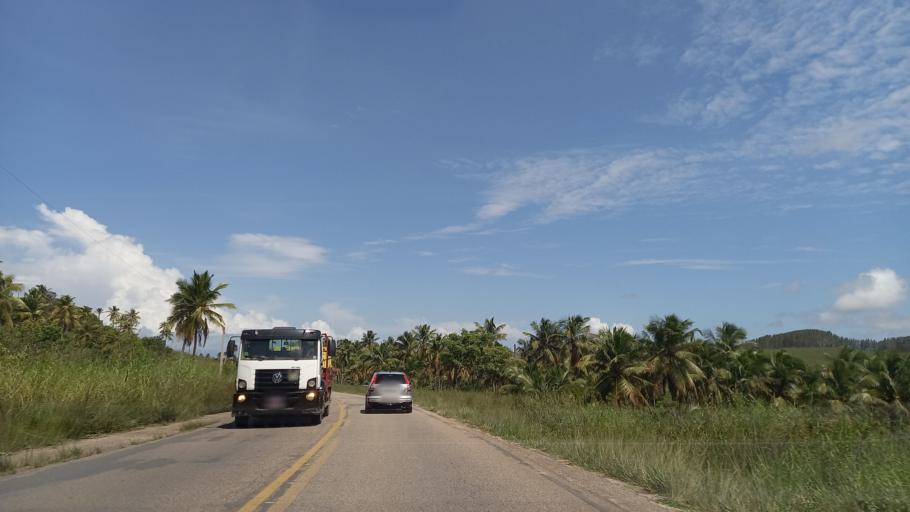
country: BR
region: Pernambuco
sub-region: Sao Jose Da Coroa Grande
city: Sao Jose da Coroa Grande
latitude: -8.8712
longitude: -35.1644
